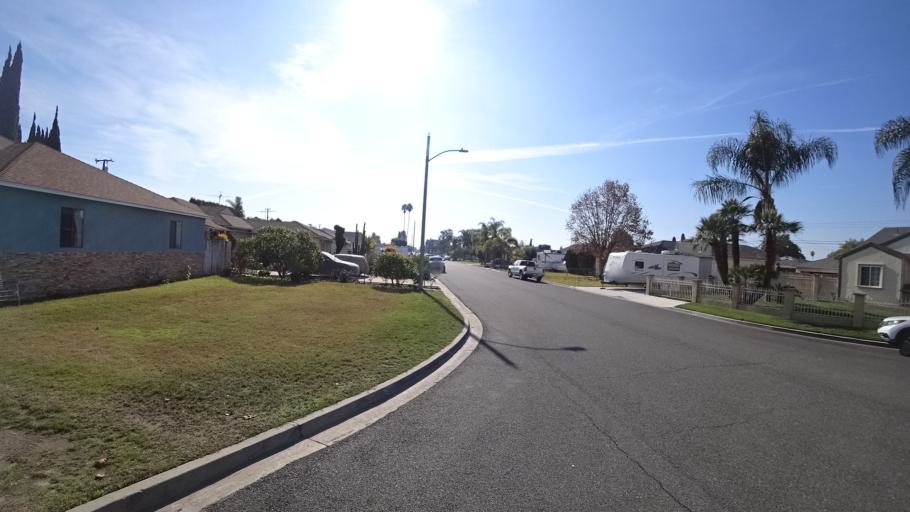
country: US
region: California
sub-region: Orange County
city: Garden Grove
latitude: 33.7976
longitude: -117.9258
